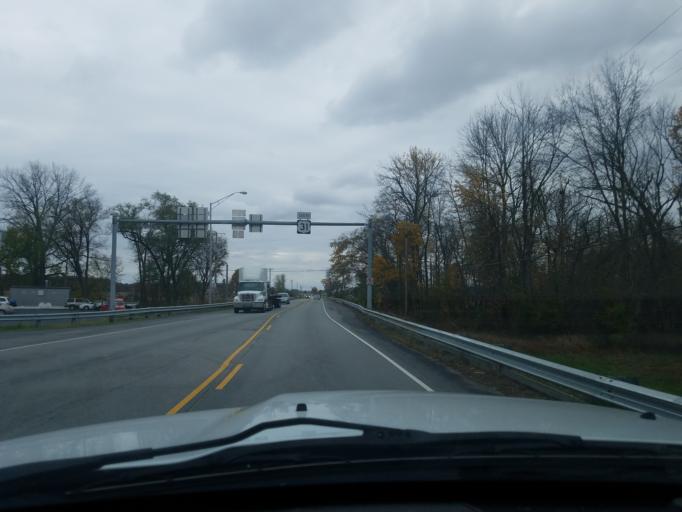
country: US
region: Indiana
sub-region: Bartholomew County
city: Columbus
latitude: 39.1664
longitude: -85.8417
